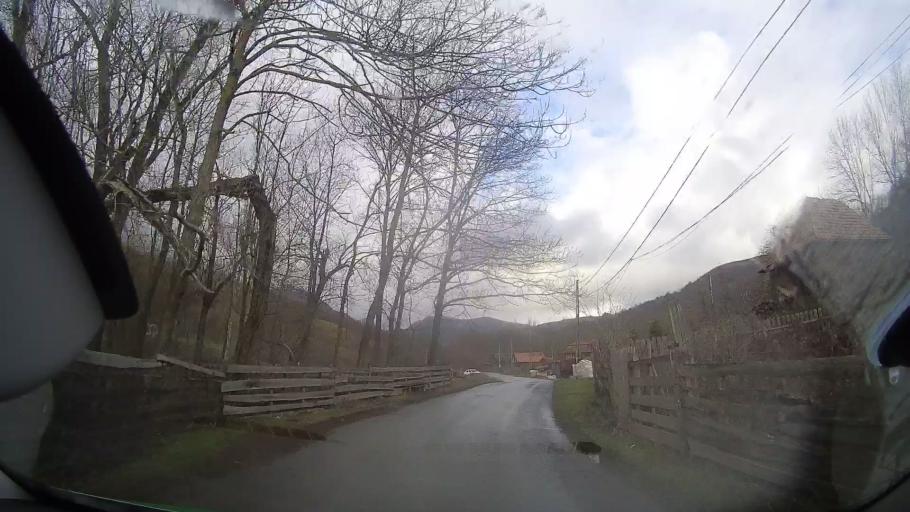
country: RO
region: Alba
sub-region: Comuna Ocolis
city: Ocolis
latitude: 46.4905
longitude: 23.4581
